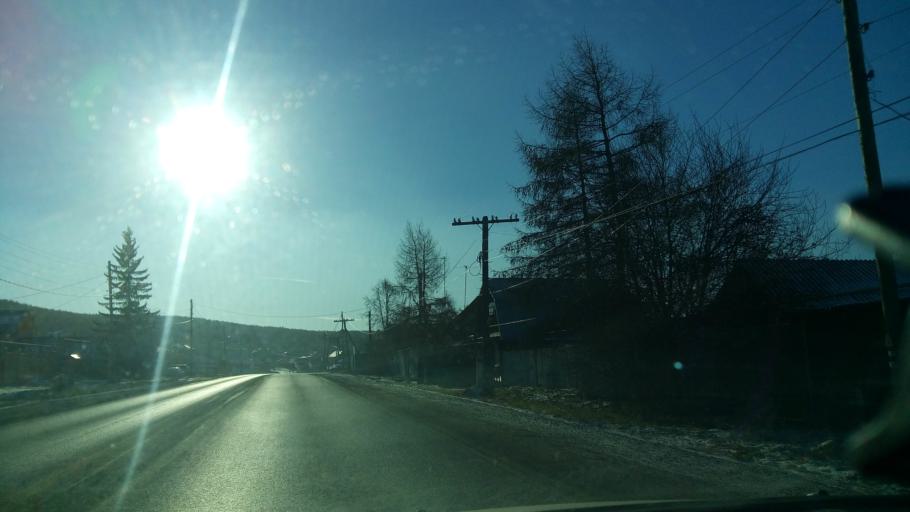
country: RU
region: Sverdlovsk
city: Gornyy Shchit
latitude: 56.6271
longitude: 60.3791
